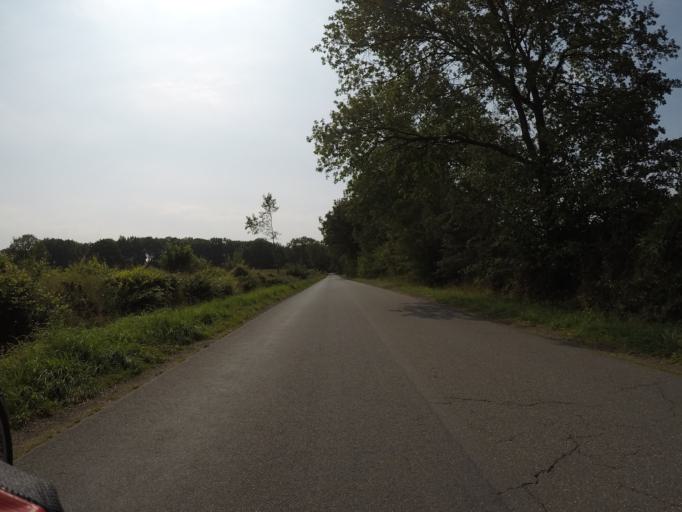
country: DE
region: Schleswig-Holstein
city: Kisdorf
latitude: 53.7754
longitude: 10.0204
